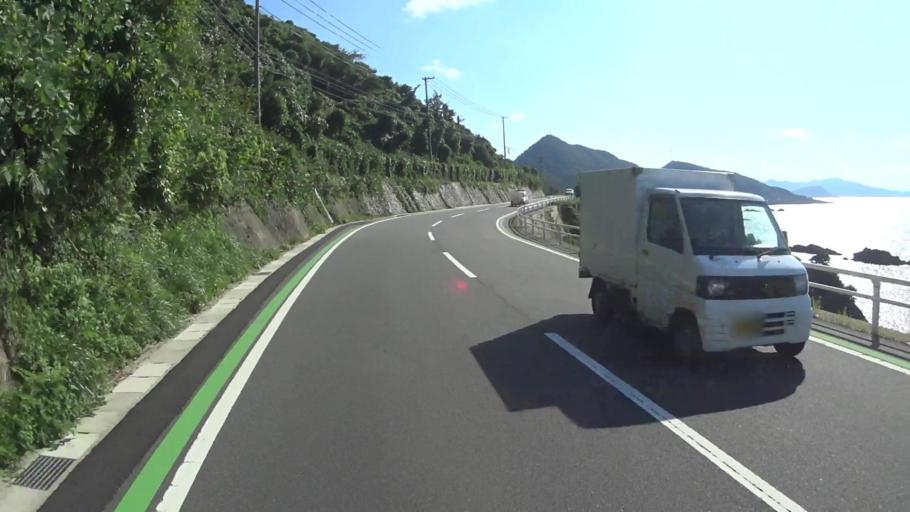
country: JP
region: Kyoto
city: Miyazu
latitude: 35.7281
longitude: 135.0871
